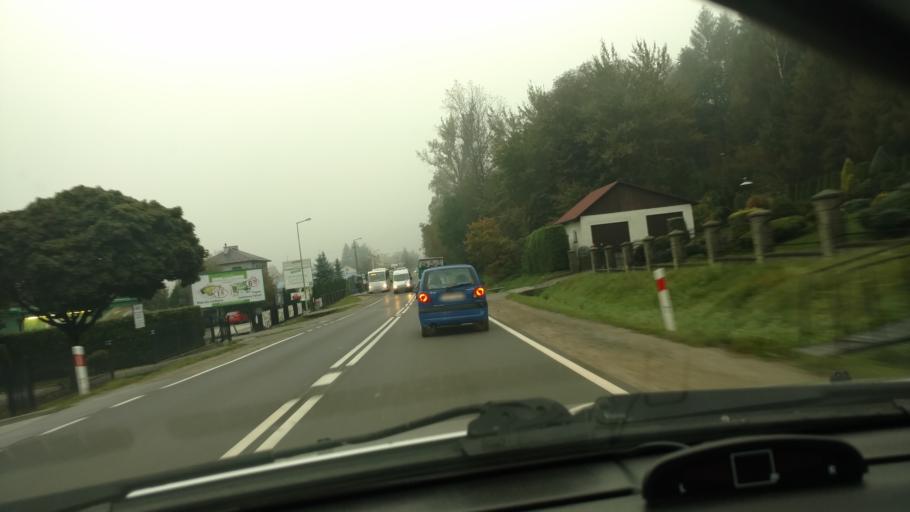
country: PL
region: Subcarpathian Voivodeship
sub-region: Powiat strzyzowski
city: Frysztak
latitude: 49.8389
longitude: 21.6100
